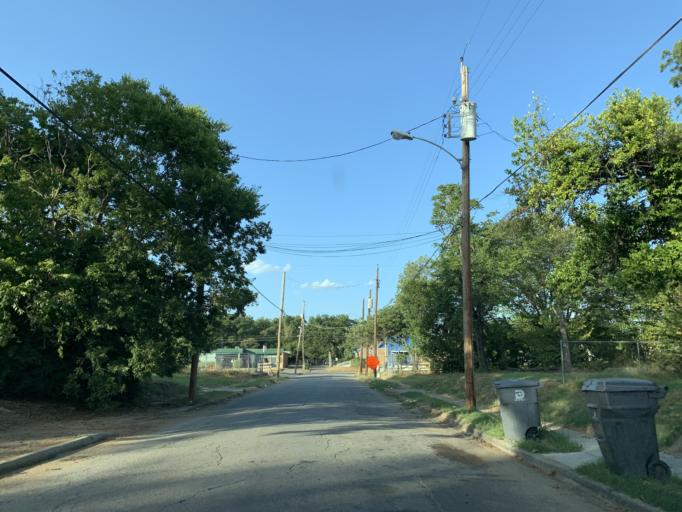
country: US
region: Texas
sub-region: Dallas County
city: Dallas
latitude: 32.7568
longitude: -96.7553
